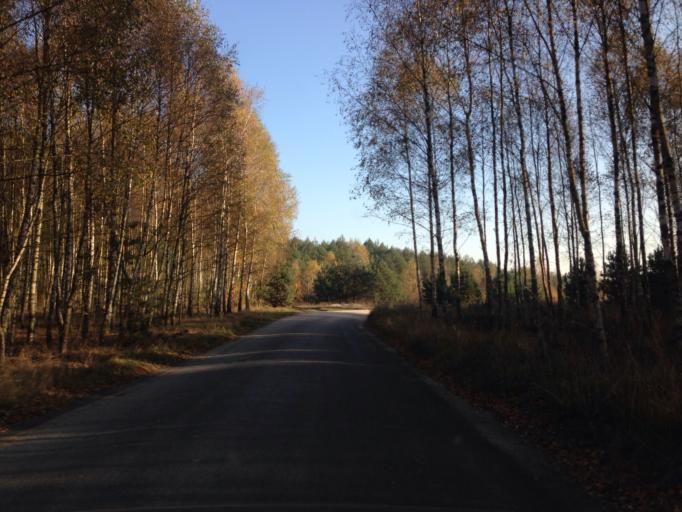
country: PL
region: Kujawsko-Pomorskie
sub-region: Powiat brodnicki
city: Gorzno
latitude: 53.1622
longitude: 19.6511
